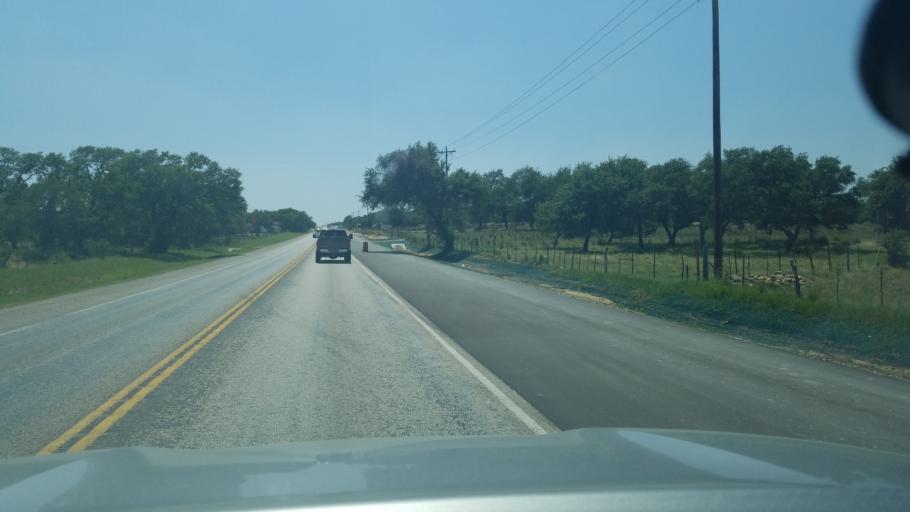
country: US
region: Texas
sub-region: Bexar County
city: Fair Oaks Ranch
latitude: 29.8182
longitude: -98.5962
